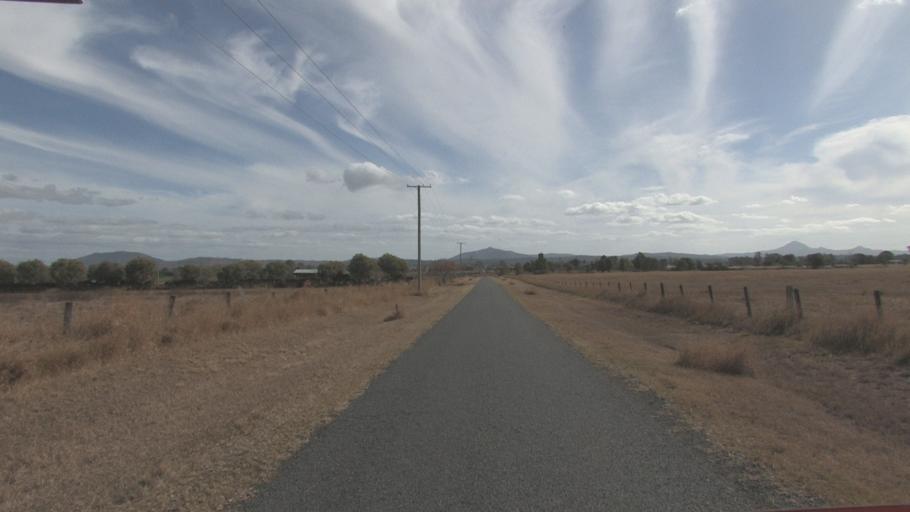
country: AU
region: Queensland
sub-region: Logan
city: Cedar Vale
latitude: -27.9230
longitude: 152.9751
